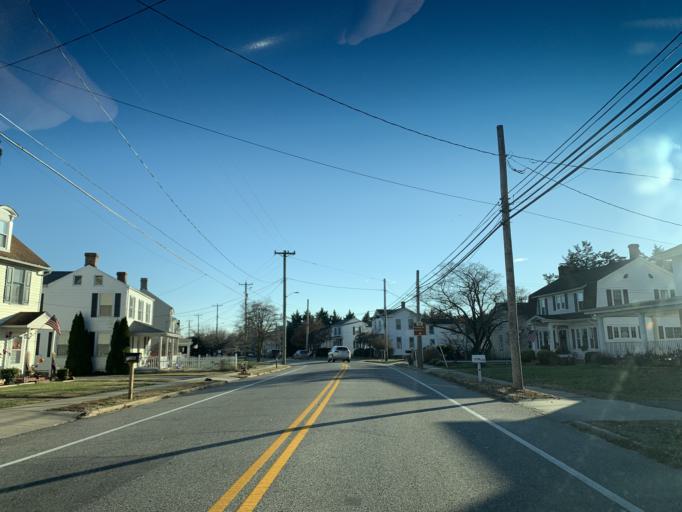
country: US
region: Delaware
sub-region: New Castle County
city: Middletown
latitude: 39.3437
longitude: -75.8794
